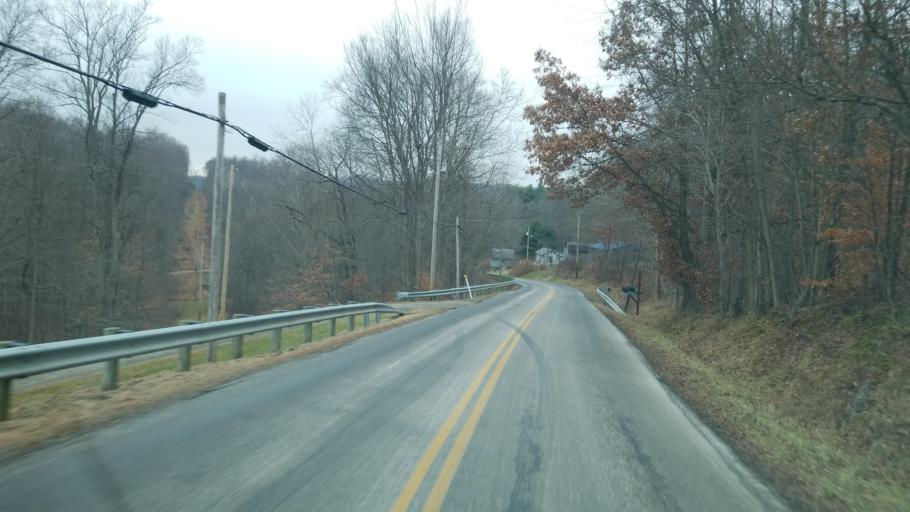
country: US
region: Ohio
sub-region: Holmes County
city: Millersburg
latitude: 40.5214
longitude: -81.9006
